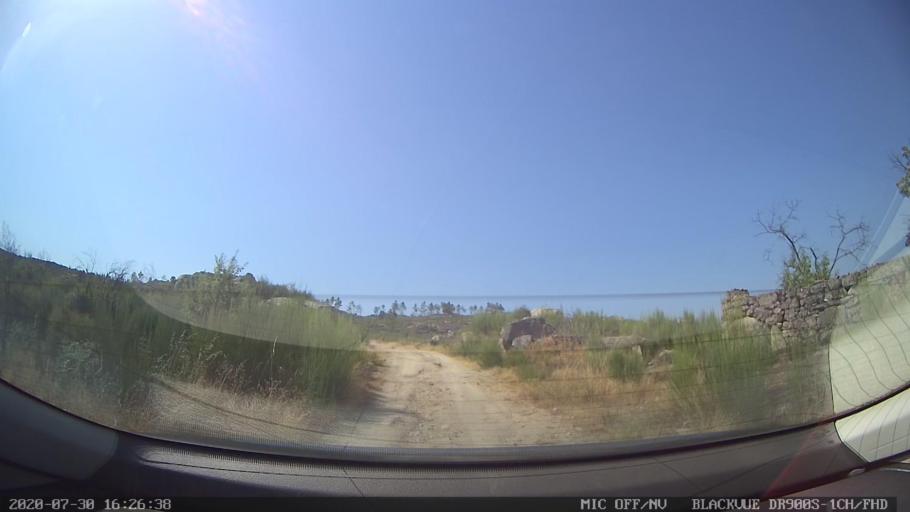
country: PT
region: Vila Real
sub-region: Sabrosa
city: Sabrosa
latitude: 41.3136
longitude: -7.4913
